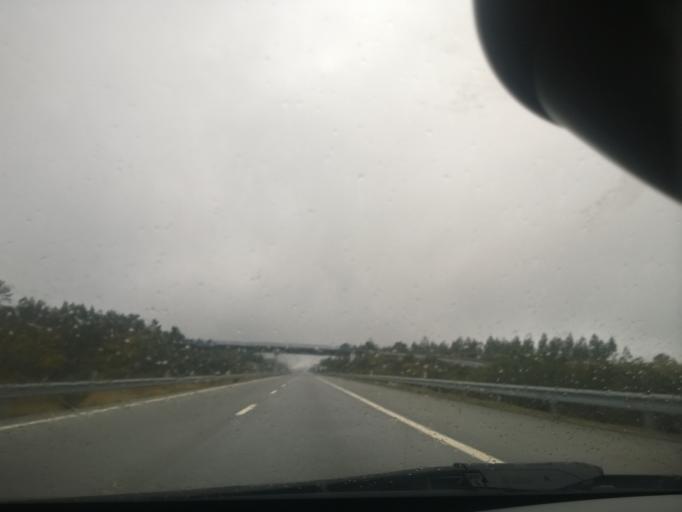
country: PT
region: Braga
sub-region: Fafe
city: Fafe
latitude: 41.4437
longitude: -8.1020
